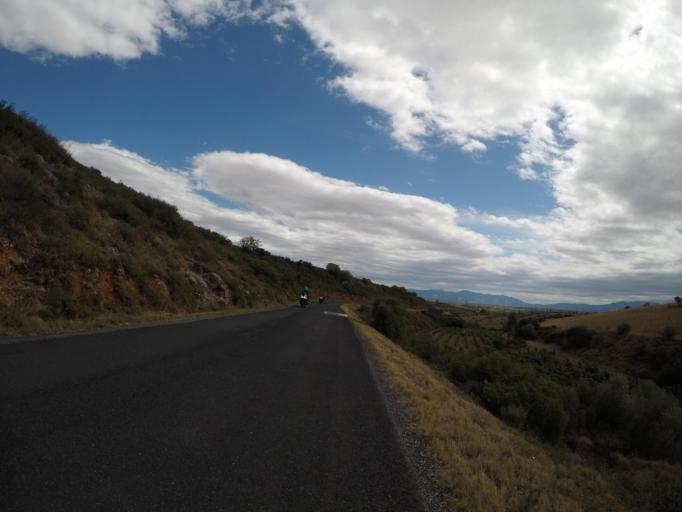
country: FR
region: Languedoc-Roussillon
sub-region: Departement des Pyrenees-Orientales
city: Baixas
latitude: 42.7534
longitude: 2.7766
